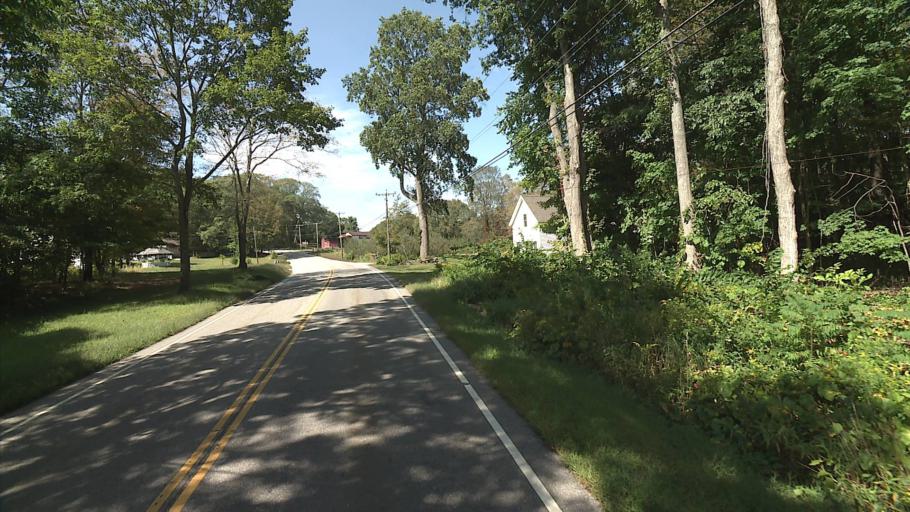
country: US
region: Connecticut
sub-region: Windham County
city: Willimantic
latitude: 41.6756
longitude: -72.2694
